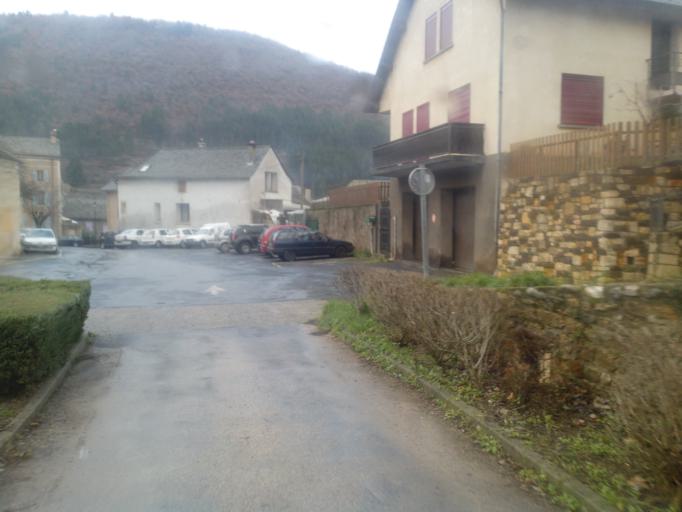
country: FR
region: Languedoc-Roussillon
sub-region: Departement de la Lozere
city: Florac
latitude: 44.3229
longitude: 3.5933
